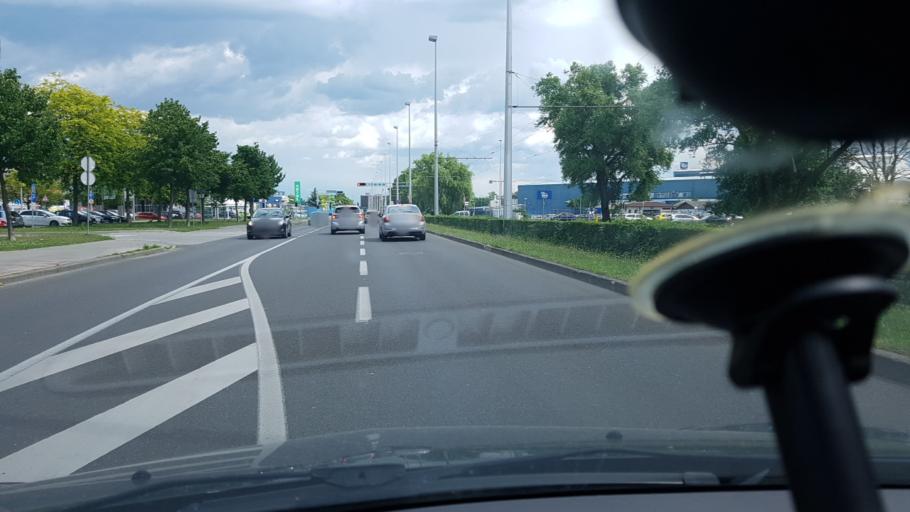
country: HR
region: Grad Zagreb
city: Dubrava
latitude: 45.8017
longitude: 16.0298
